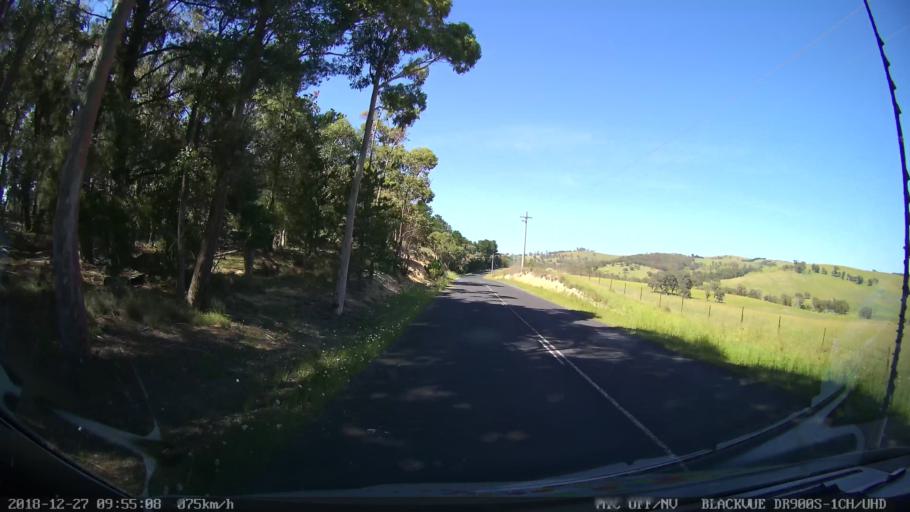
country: AU
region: New South Wales
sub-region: Lithgow
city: Portland
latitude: -33.3988
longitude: 149.9789
